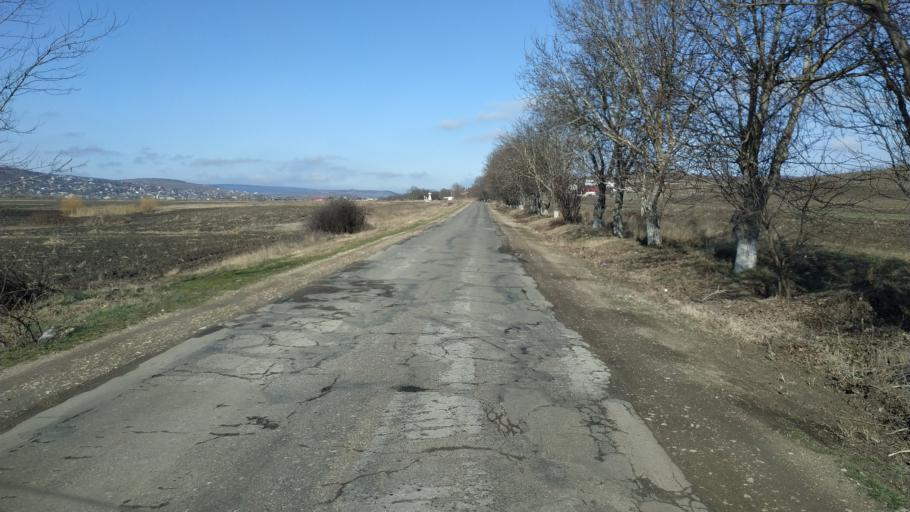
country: MD
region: Laloveni
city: Ialoveni
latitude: 46.9258
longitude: 28.6787
